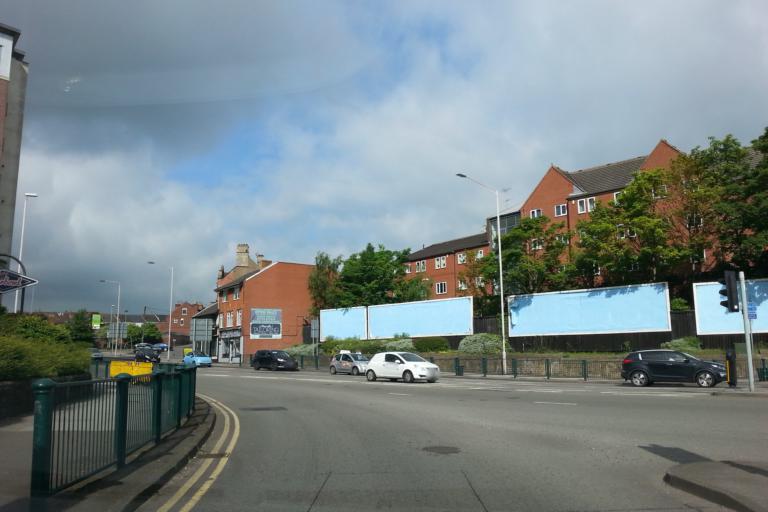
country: GB
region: England
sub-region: Nottinghamshire
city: Mansfield
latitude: 53.1434
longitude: -1.2011
